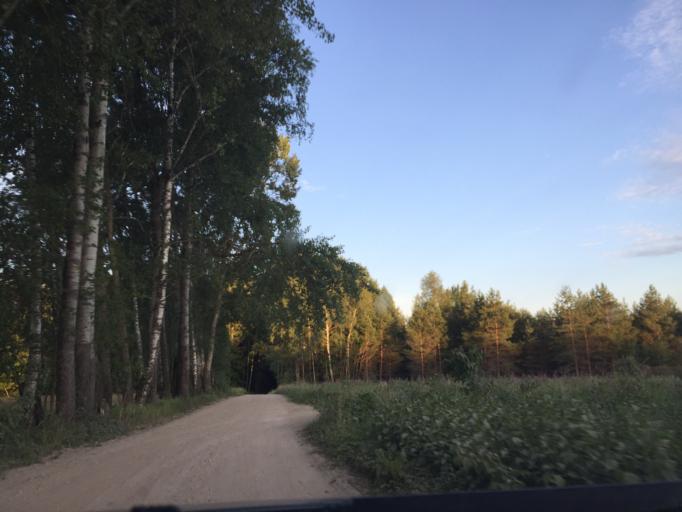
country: LV
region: Koknese
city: Koknese
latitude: 56.6209
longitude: 25.4920
